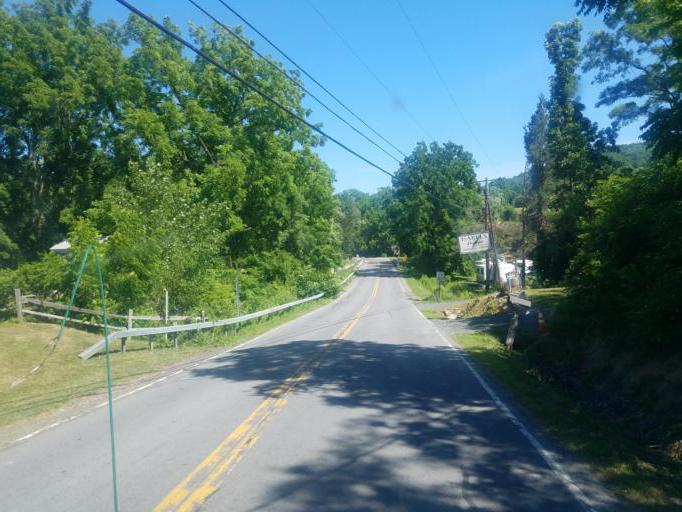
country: US
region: New York
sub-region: Ontario County
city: Naples
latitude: 42.7238
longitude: -77.3243
